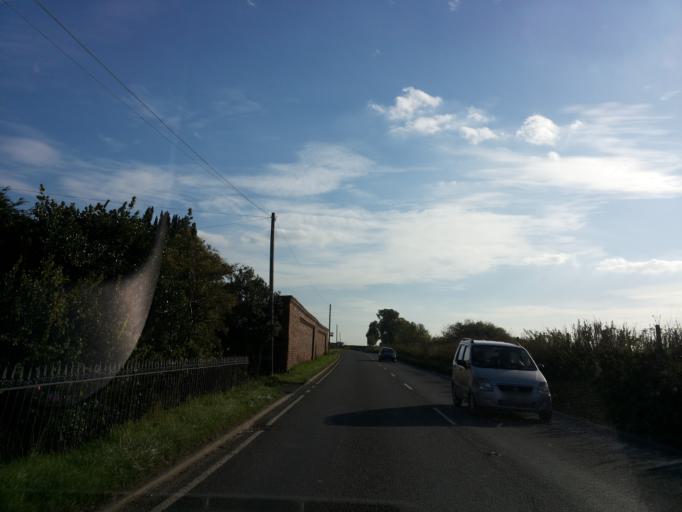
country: GB
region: England
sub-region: East Riding of Yorkshire
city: Rawcliffe
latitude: 53.6607
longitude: -0.9898
